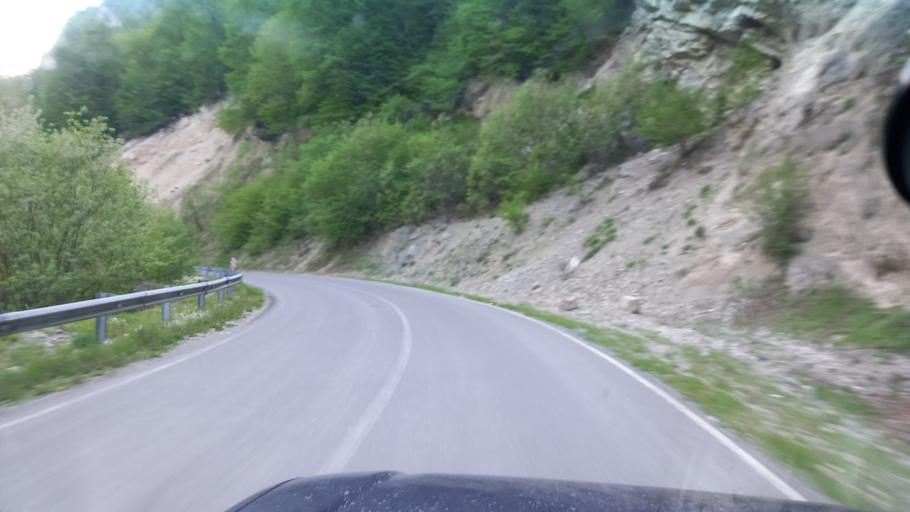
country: RU
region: Ingushetiya
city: Galashki
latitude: 42.9263
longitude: 45.0073
